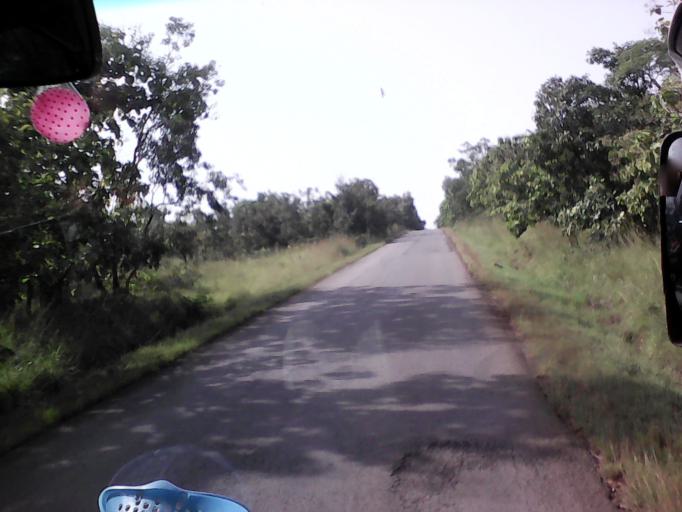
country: TG
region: Centrale
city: Sokode
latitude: 9.1278
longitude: 1.1473
